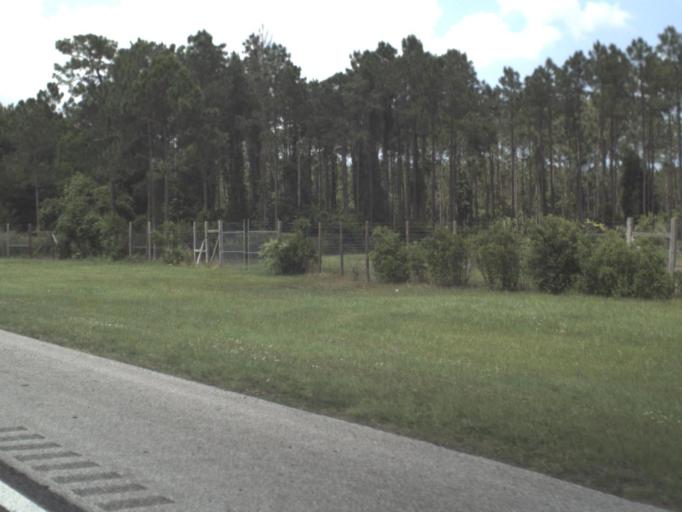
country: US
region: Florida
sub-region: Saint Johns County
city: Saint Augustine Shores
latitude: 29.7595
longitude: -81.3510
